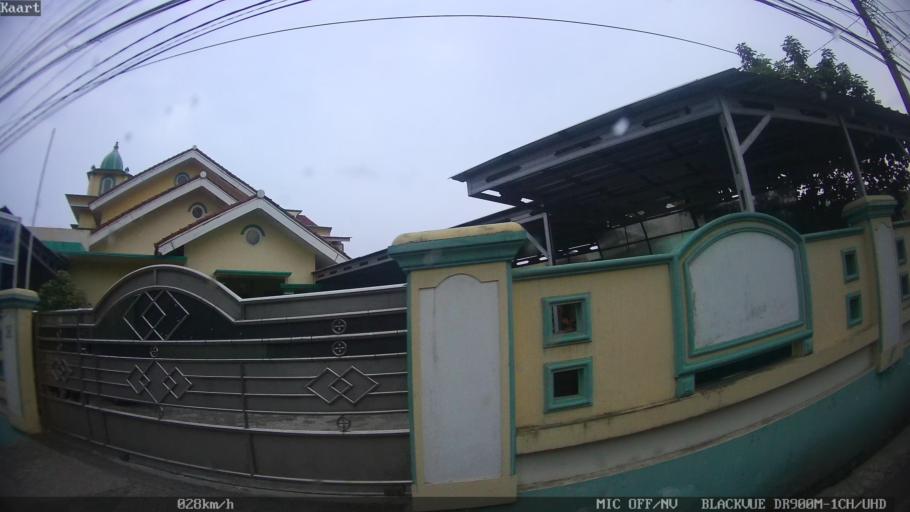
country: ID
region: Lampung
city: Kedaton
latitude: -5.3991
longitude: 105.2659
